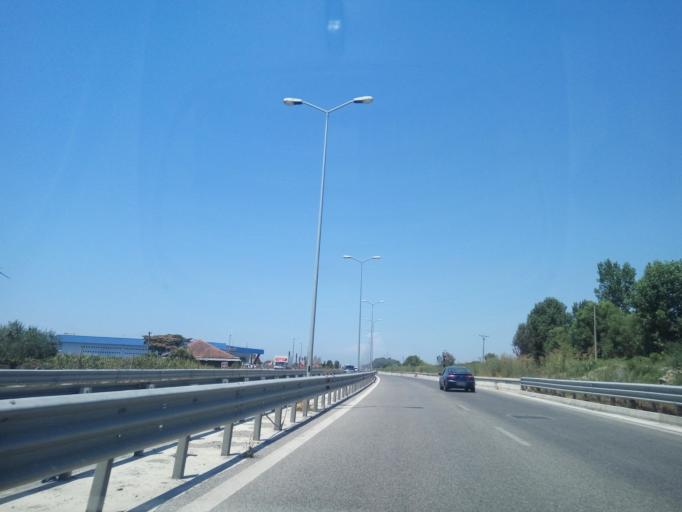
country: AL
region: Tirane
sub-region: Rrethi i Tiranes
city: Shengjergj
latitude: 41.2080
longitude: 19.5341
